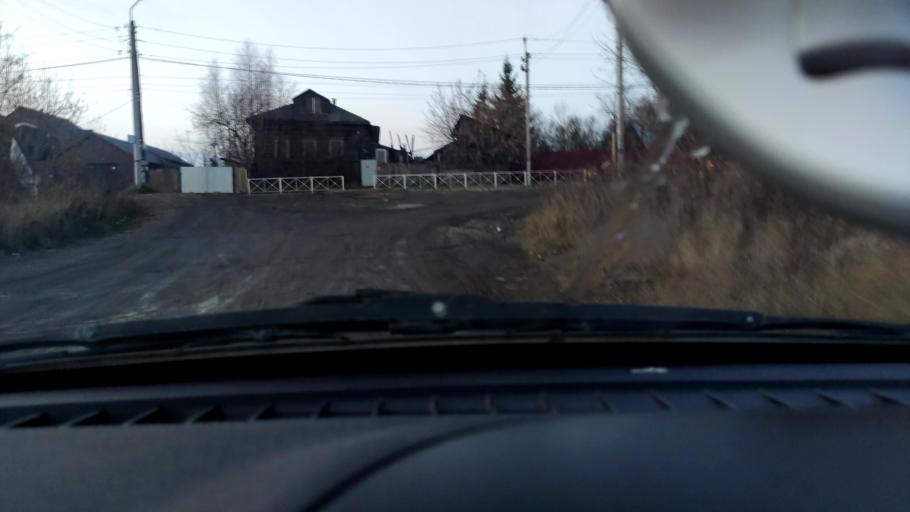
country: RU
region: Perm
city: Perm
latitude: 58.0274
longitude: 56.2169
